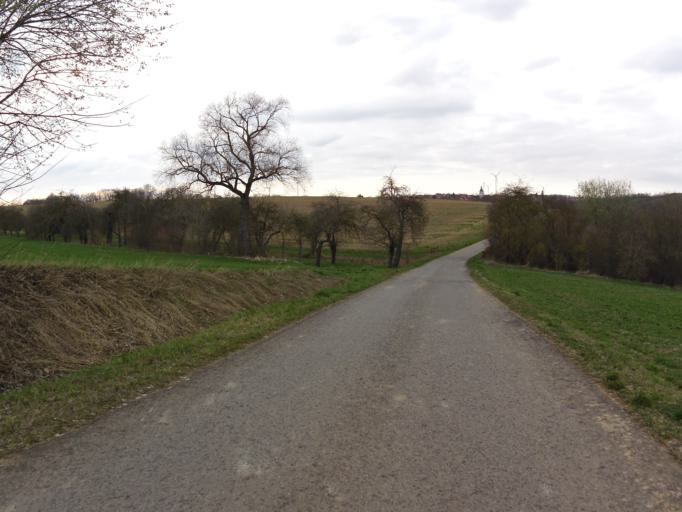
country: DE
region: Bavaria
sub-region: Regierungsbezirk Unterfranken
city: Buchbrunn
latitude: 49.7440
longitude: 10.1291
